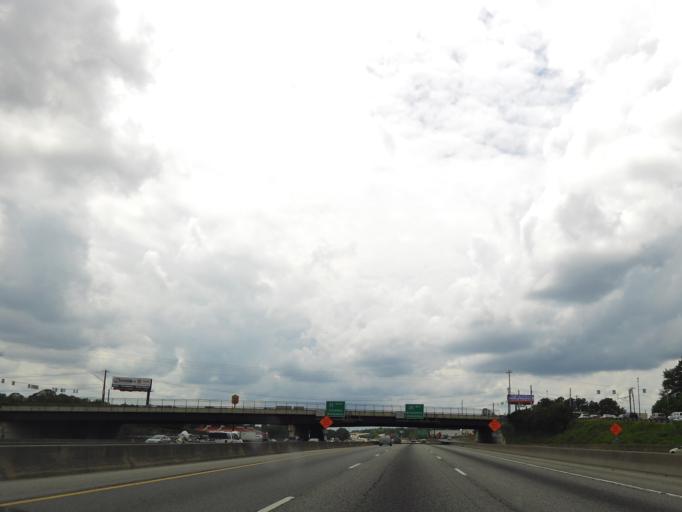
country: US
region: Georgia
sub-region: Fulton County
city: College Park
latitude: 33.6207
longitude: -84.4723
